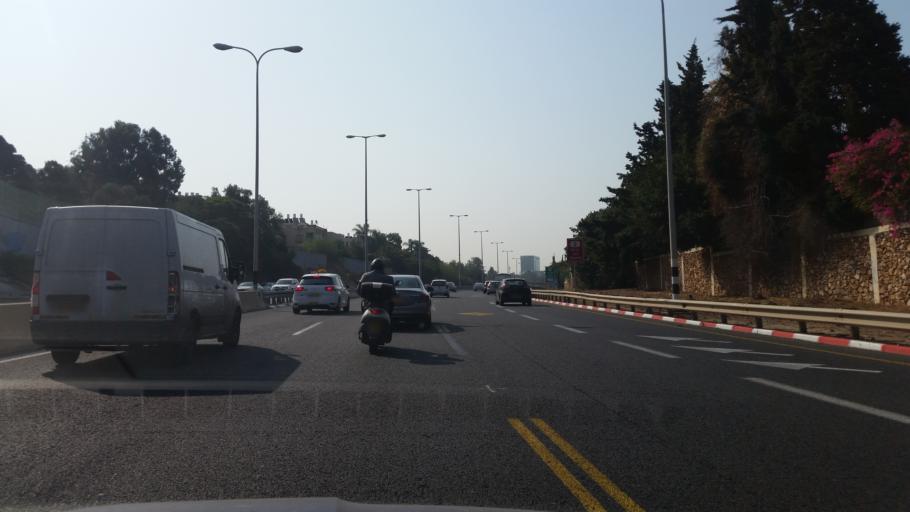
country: IL
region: Tel Aviv
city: Kefar Shemaryahu
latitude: 32.1751
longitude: 34.8159
